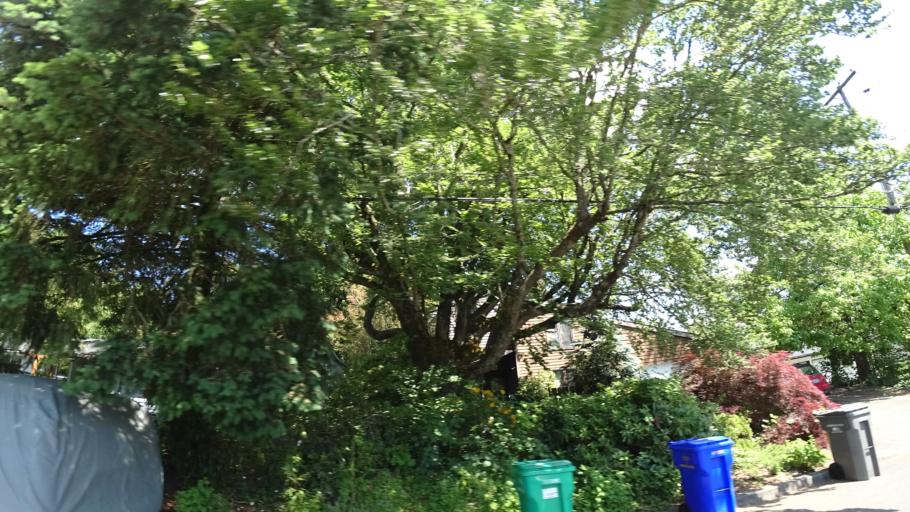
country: US
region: Oregon
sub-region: Washington County
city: Garden Home-Whitford
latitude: 45.4698
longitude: -122.7026
